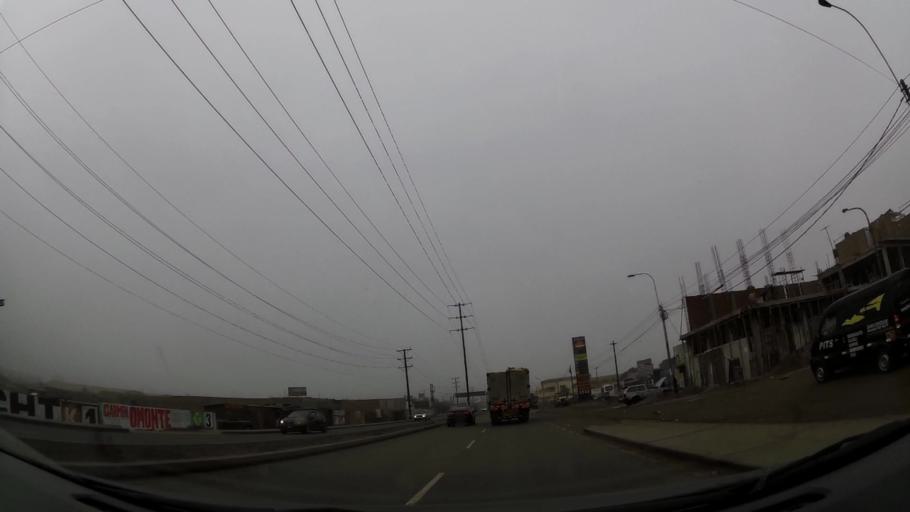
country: PE
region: Lima
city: Ventanilla
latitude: -11.8409
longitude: -77.1142
